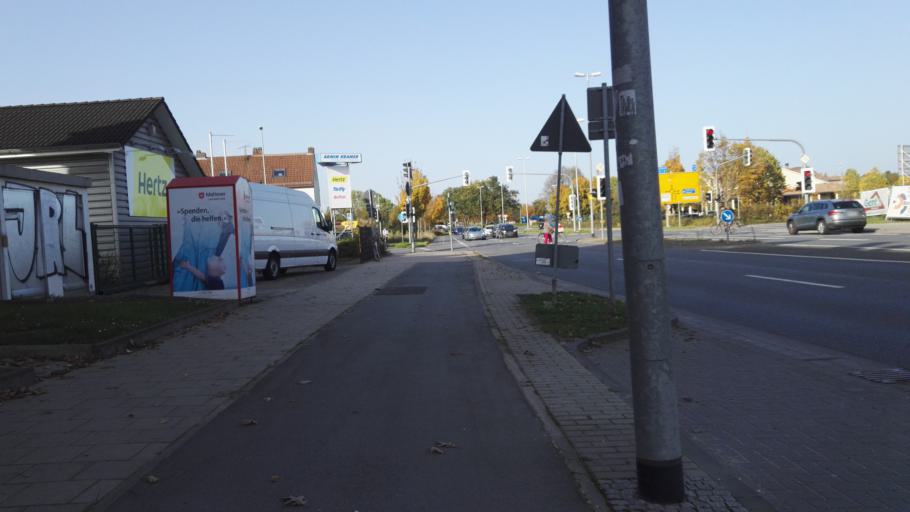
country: DE
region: Lower Saxony
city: Hildesheim
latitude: 52.1559
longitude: 9.9722
